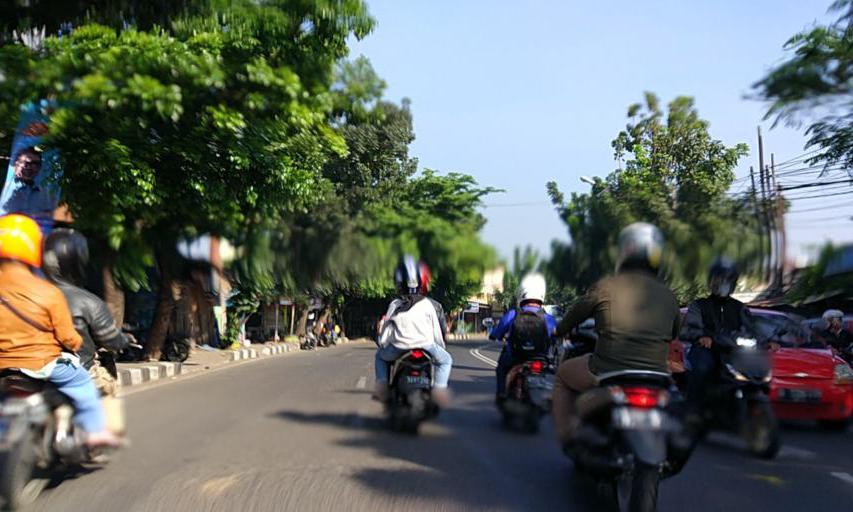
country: ID
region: West Java
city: Bandung
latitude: -6.9016
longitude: 107.6481
